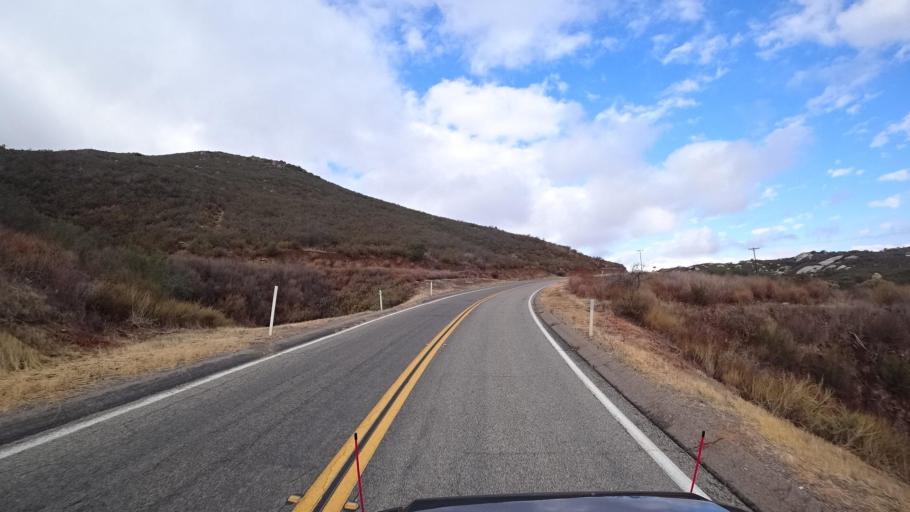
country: MX
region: Baja California
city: Tecate
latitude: 32.6263
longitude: -116.6290
